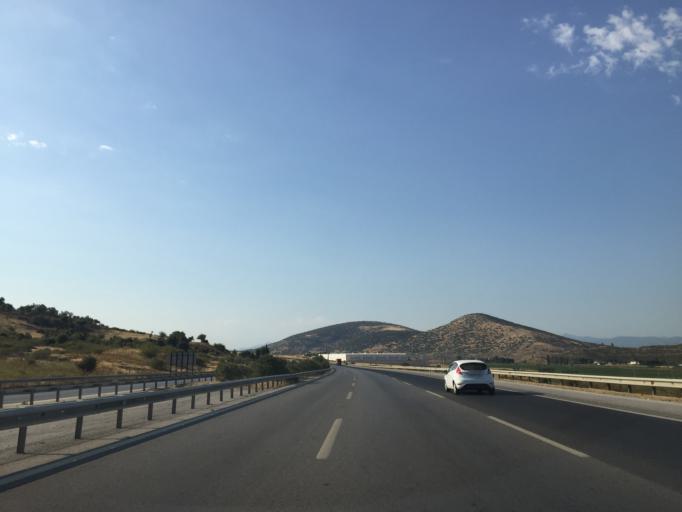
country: TR
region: Izmir
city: Belevi
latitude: 38.0454
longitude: 27.4287
